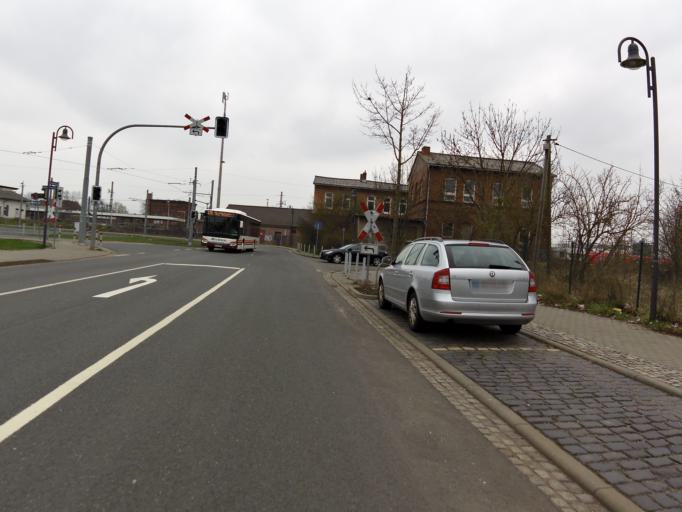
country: DE
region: Thuringia
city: Gotha
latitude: 50.9400
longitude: 10.7101
